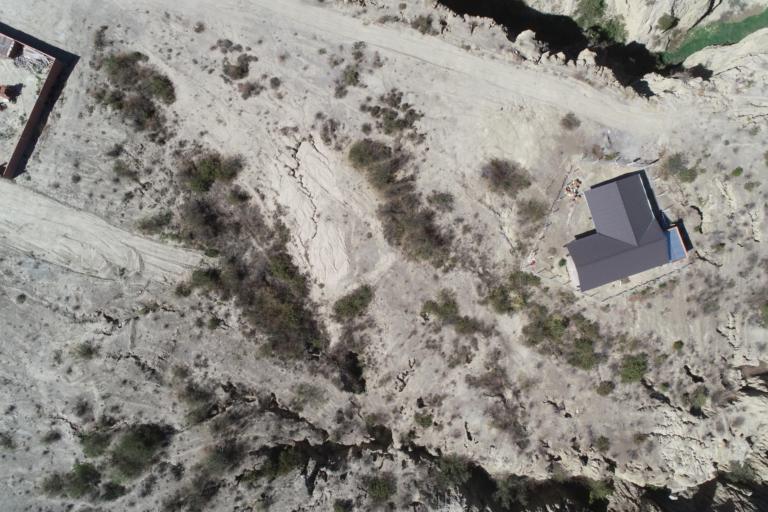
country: BO
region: La Paz
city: La Paz
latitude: -16.6361
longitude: -68.0499
